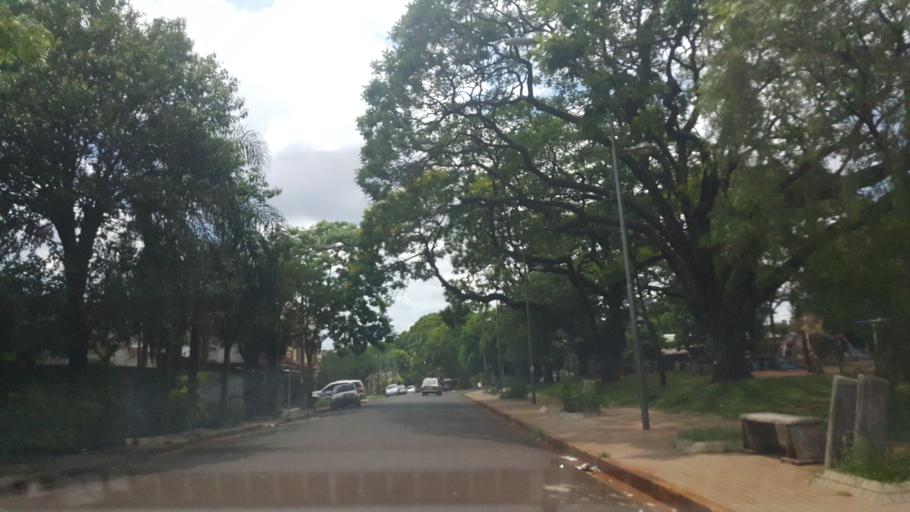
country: AR
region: Misiones
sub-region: Departamento de Capital
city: Posadas
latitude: -27.3841
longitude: -55.8942
